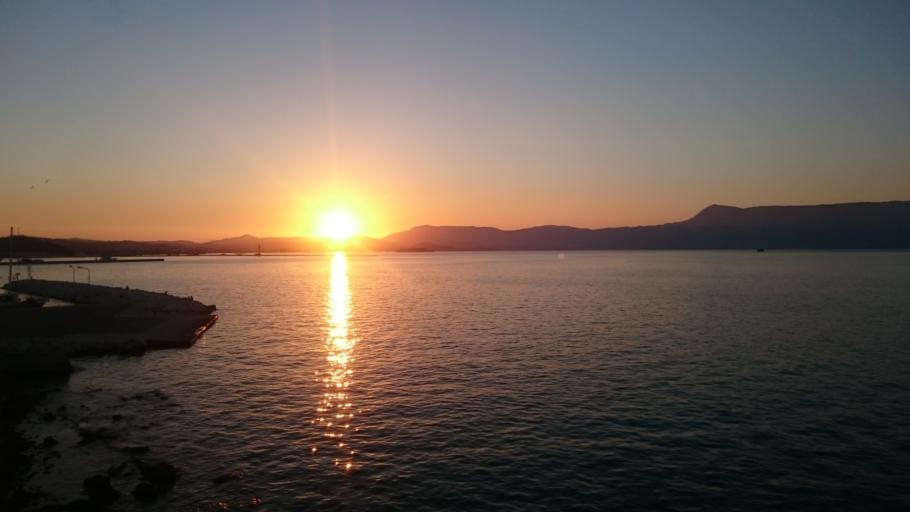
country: GR
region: Ionian Islands
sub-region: Nomos Kerkyras
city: Kerkyra
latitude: 39.6276
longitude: 19.9219
